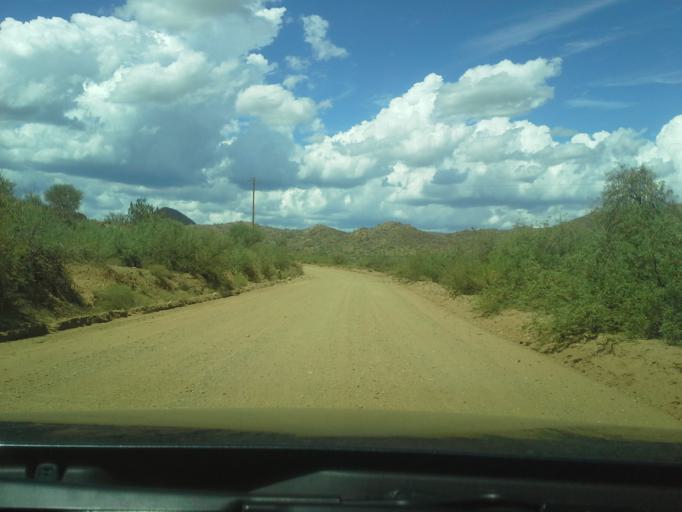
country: US
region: Arizona
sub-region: Yavapai County
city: Spring Valley
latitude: 34.2625
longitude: -112.1813
